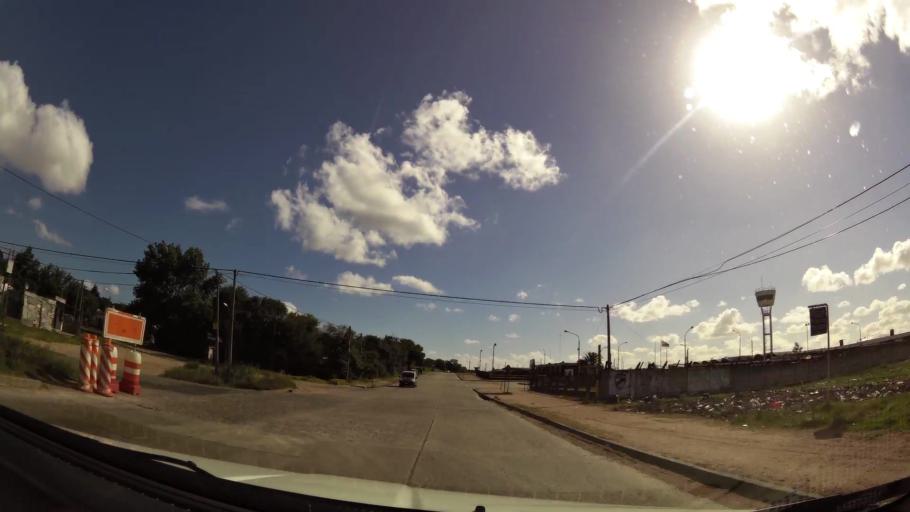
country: UY
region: Canelones
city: La Paz
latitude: -34.8207
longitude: -56.2384
